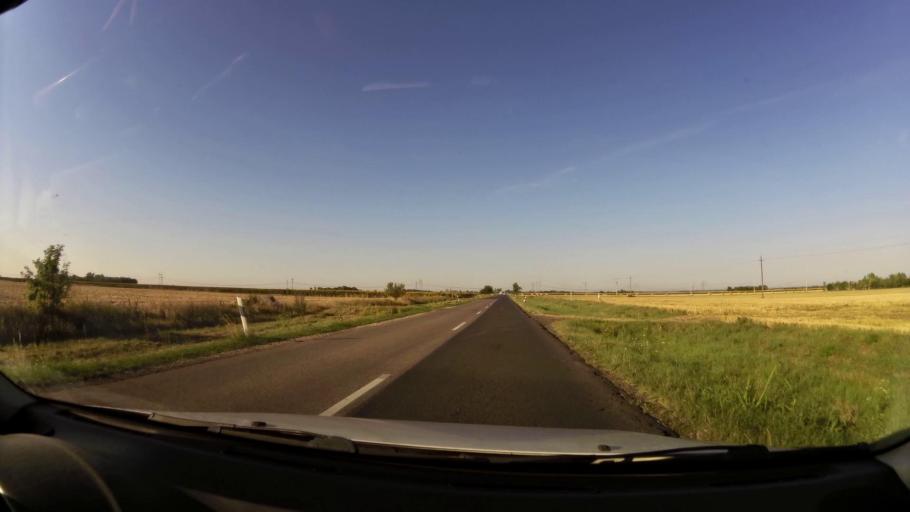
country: HU
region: Pest
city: Tapioszolos
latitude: 47.2456
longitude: 19.8454
